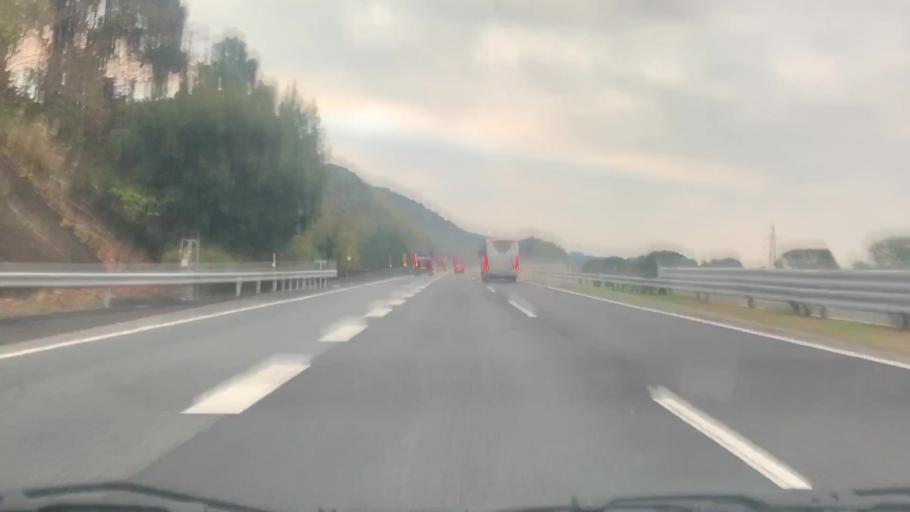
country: JP
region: Nagasaki
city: Omura
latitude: 32.9922
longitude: 129.9544
